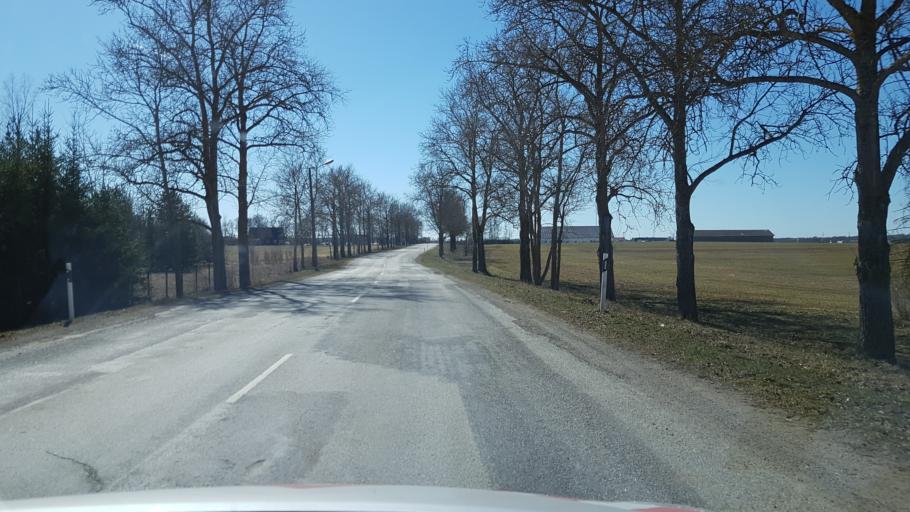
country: EE
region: Laeaene-Virumaa
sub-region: Rakvere linn
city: Rakvere
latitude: 59.3687
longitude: 26.3776
